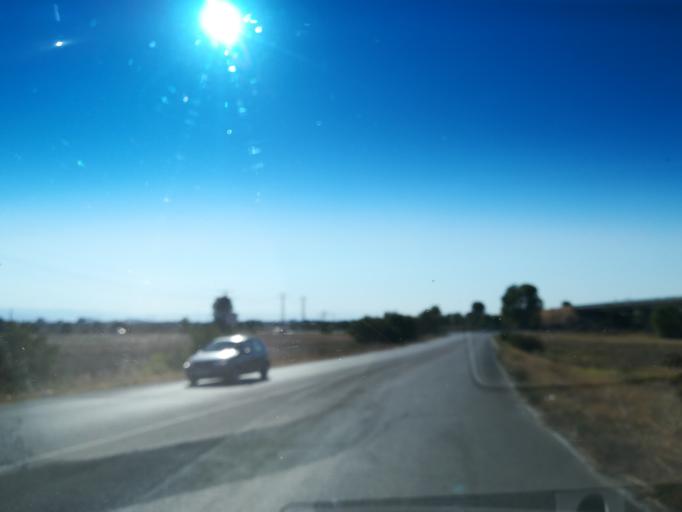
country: BG
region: Plovdiv
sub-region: Obshtina Plovdiv
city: Plovdiv
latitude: 42.1719
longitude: 24.8219
